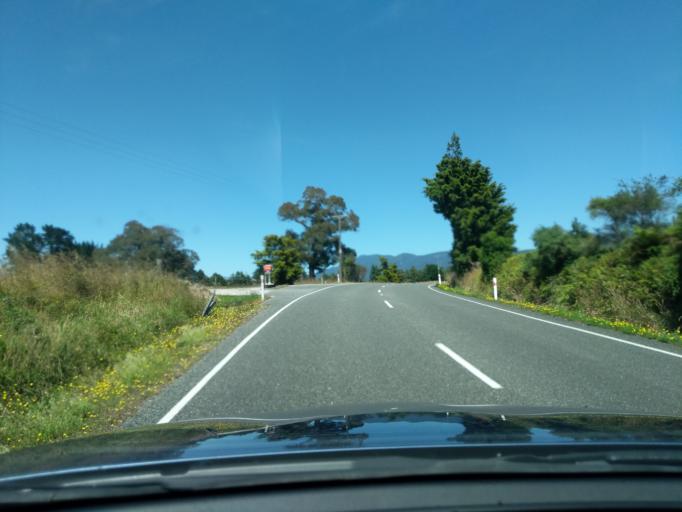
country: NZ
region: Tasman
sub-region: Tasman District
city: Takaka
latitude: -40.6838
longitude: 172.6610
